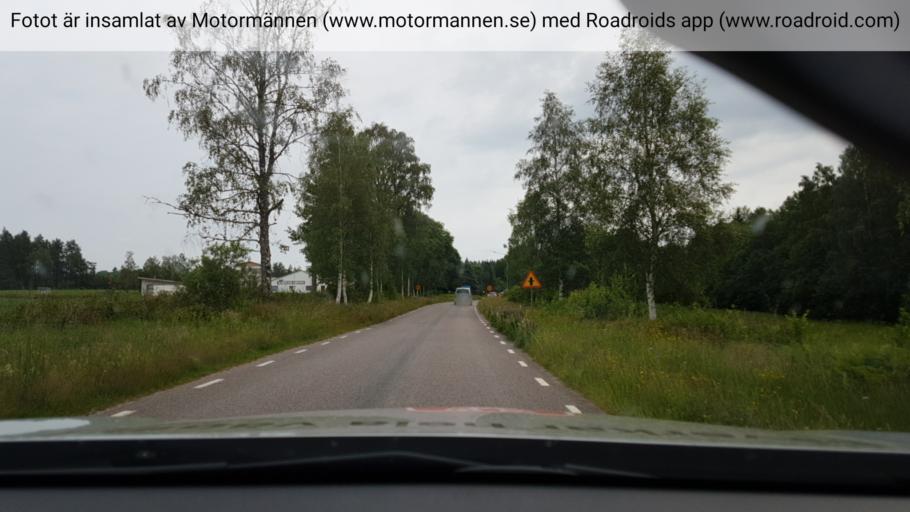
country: SE
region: Vaestra Goetaland
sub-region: Tidaholms Kommun
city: Tidaholm
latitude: 58.0703
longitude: 13.9421
